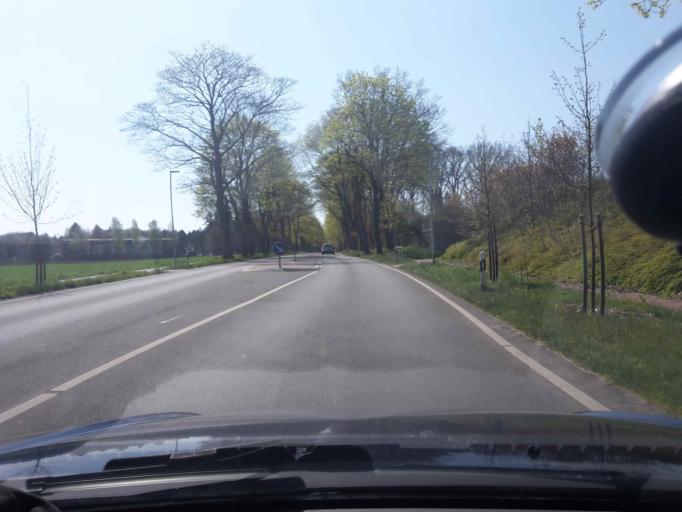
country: DE
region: Lower Saxony
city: Welle
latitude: 53.2349
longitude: 9.8035
